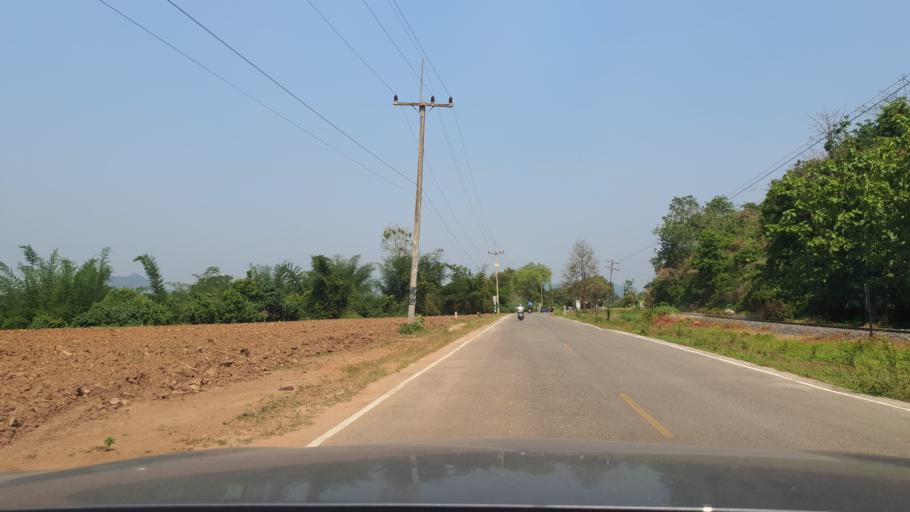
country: TH
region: Kanchanaburi
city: Sai Yok
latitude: 14.0945
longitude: 99.1773
